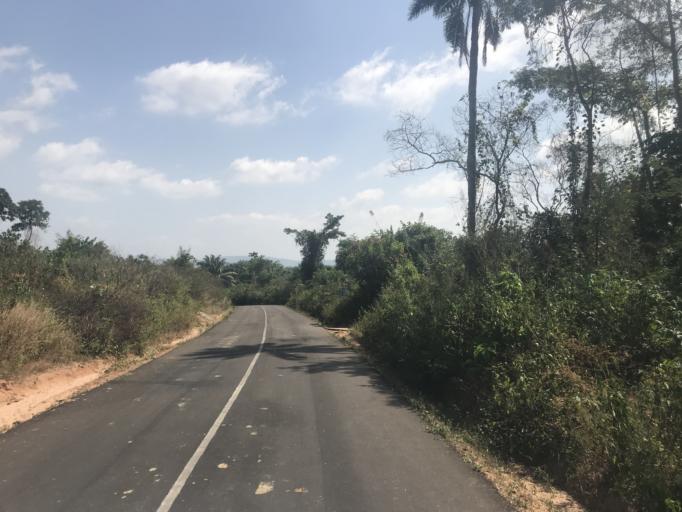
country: NG
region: Osun
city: Otan Ayegbaju
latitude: 7.8928
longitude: 4.8508
